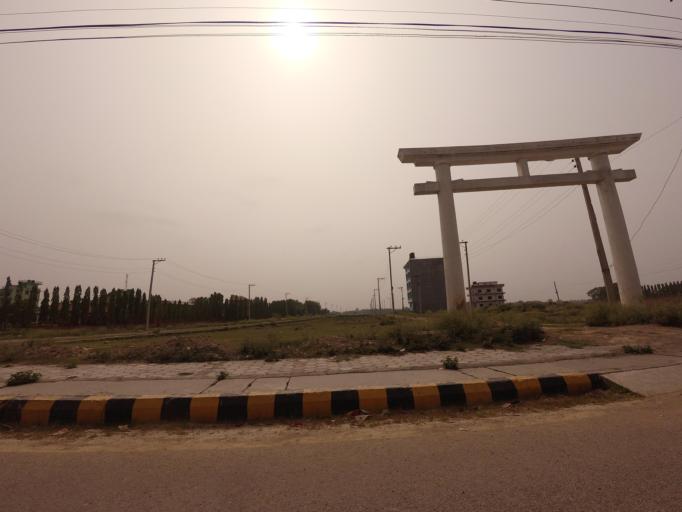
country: IN
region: Uttar Pradesh
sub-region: Maharajganj
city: Nautanwa
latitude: 27.4680
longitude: 83.2839
